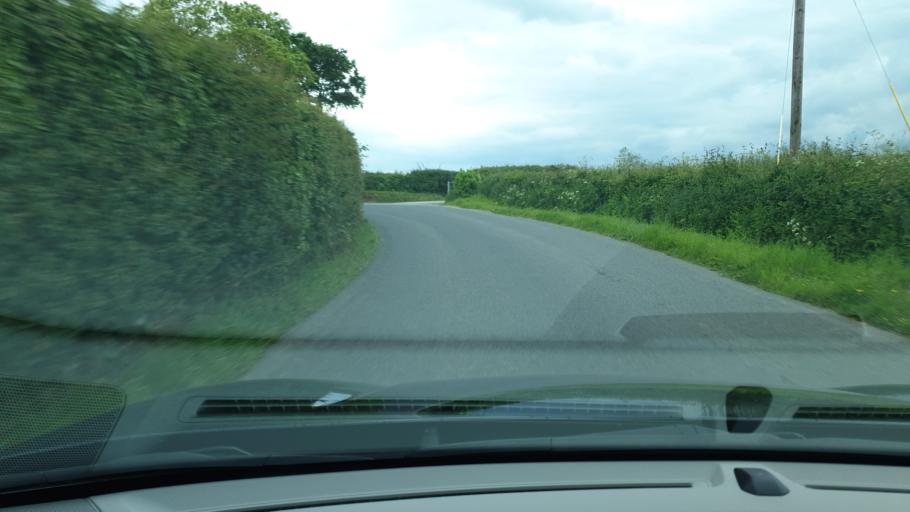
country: IE
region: Leinster
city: Lusk
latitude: 53.5585
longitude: -6.1701
